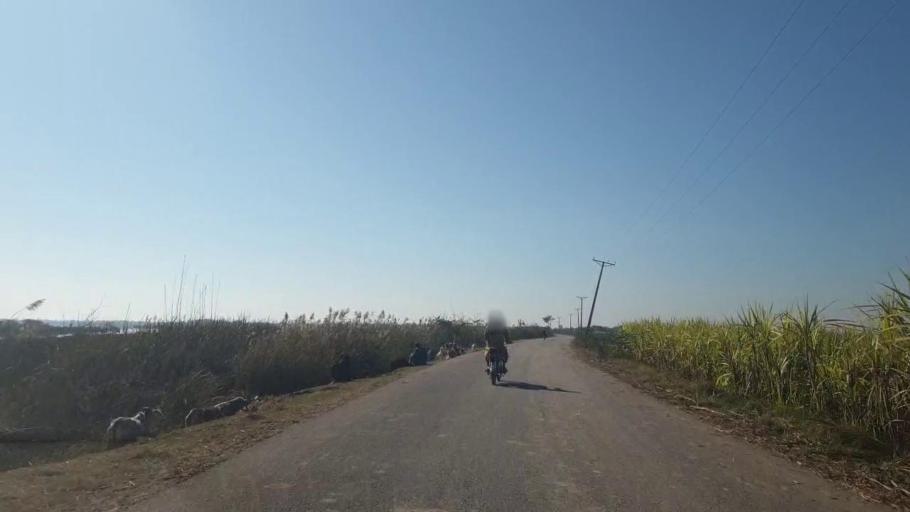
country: PK
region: Sindh
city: Kot Diji
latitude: 27.3056
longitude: 68.6457
